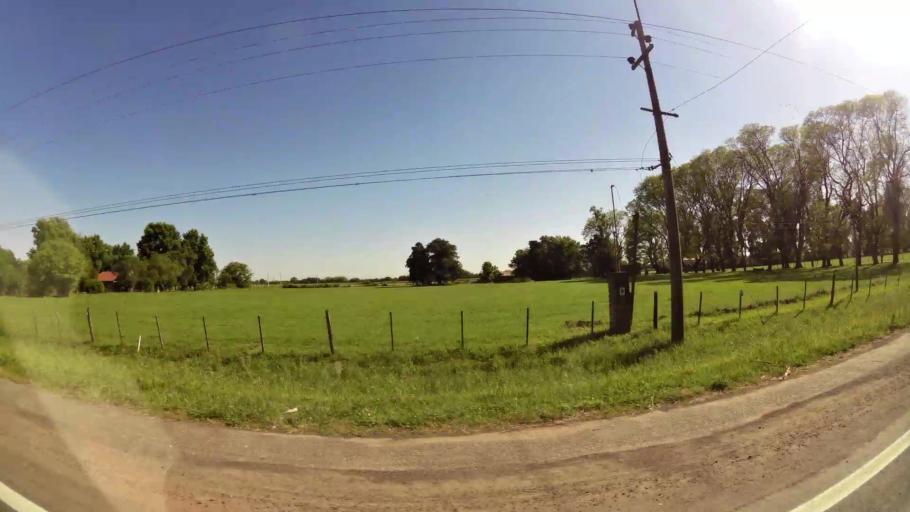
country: AR
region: Santa Fe
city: Esperanza
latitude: -31.4496
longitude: -60.9013
